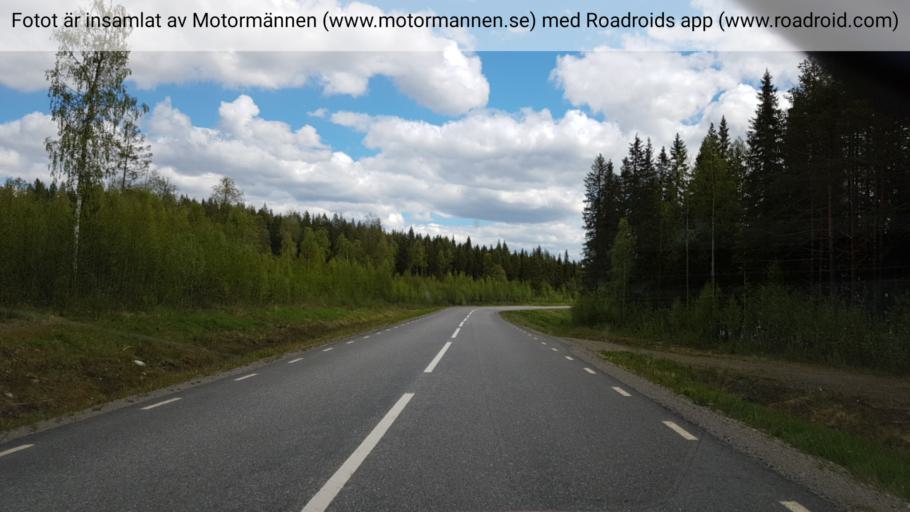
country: SE
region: Vaesterbotten
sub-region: Norsjo Kommun
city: Norsjoe
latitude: 64.8371
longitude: 19.8065
